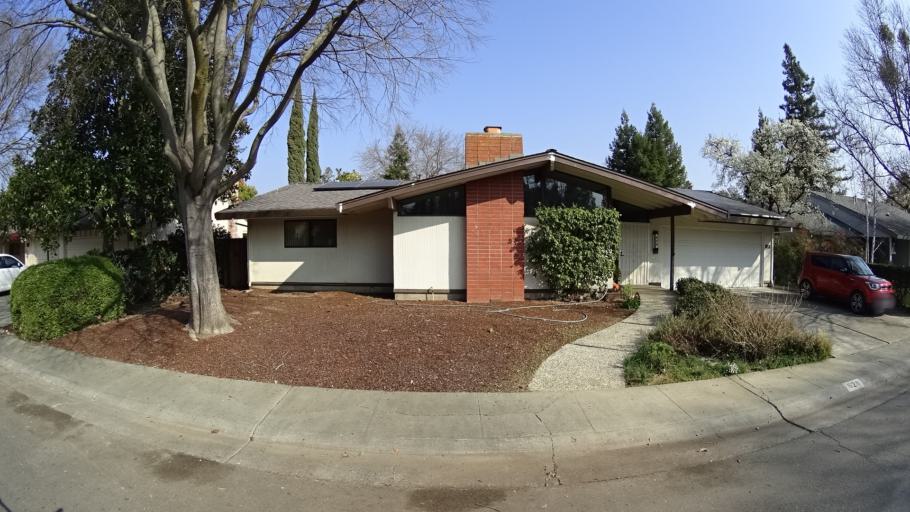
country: US
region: California
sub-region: Yolo County
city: Davis
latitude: 38.5483
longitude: -121.7765
